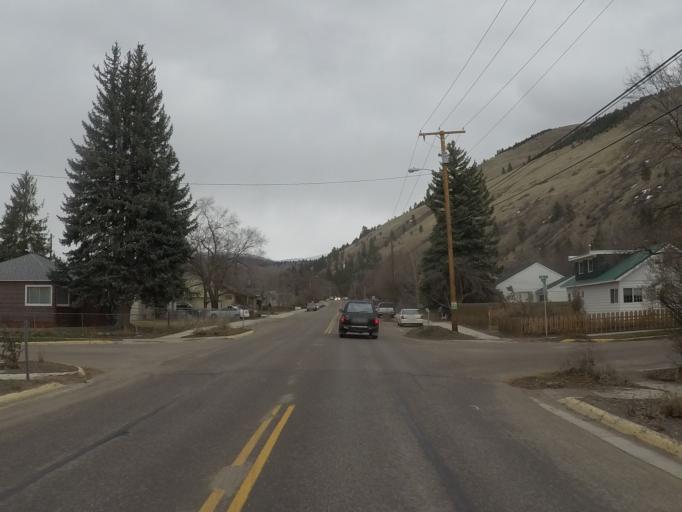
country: US
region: Montana
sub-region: Missoula County
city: Missoula
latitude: 46.8733
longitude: -113.9772
